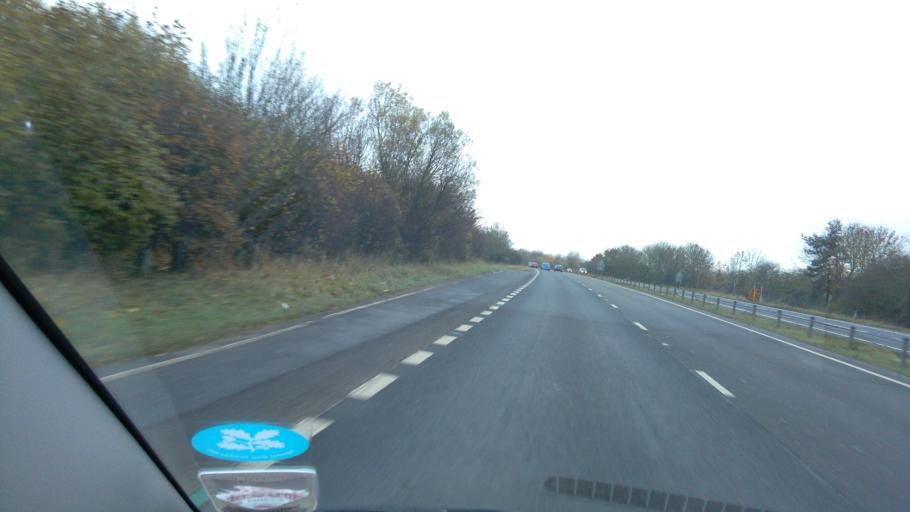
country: GB
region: England
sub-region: Northamptonshire
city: Towcester
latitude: 52.1229
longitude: -1.0059
